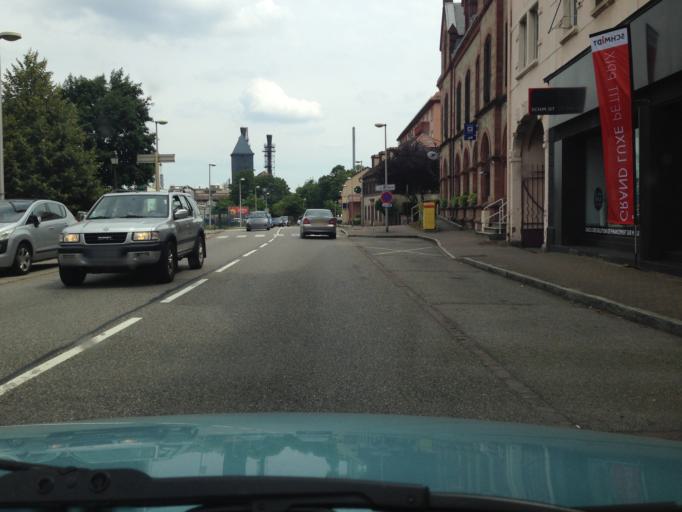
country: FR
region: Alsace
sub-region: Departement du Haut-Rhin
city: Vieux-Thann
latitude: 47.8087
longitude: 7.1066
